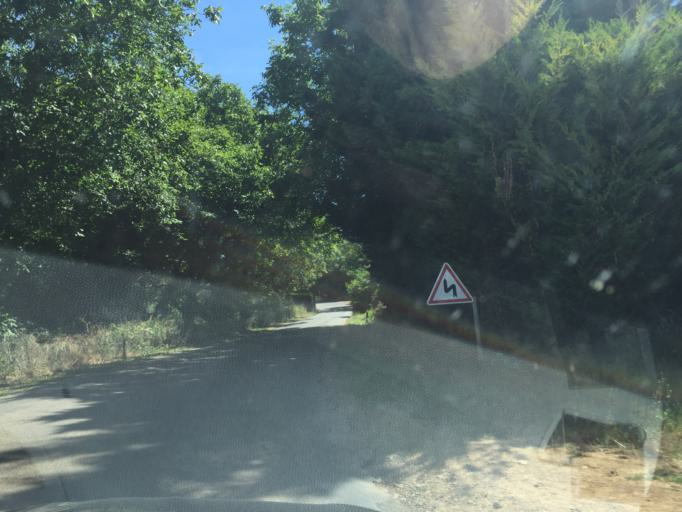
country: FR
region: Poitou-Charentes
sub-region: Departement de la Vienne
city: Vivonne
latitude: 46.4389
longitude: 0.3020
